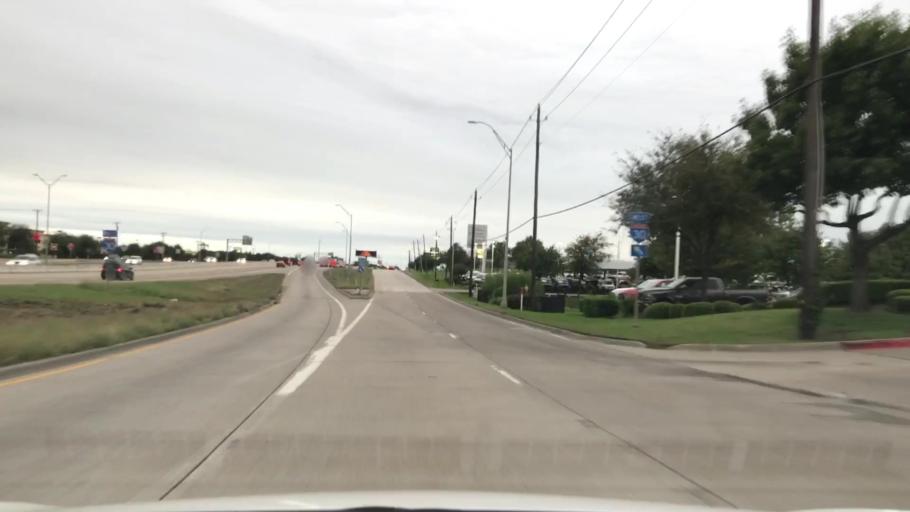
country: US
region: Texas
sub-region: Rockwall County
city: Rockwall
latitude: 32.9068
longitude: -96.4526
